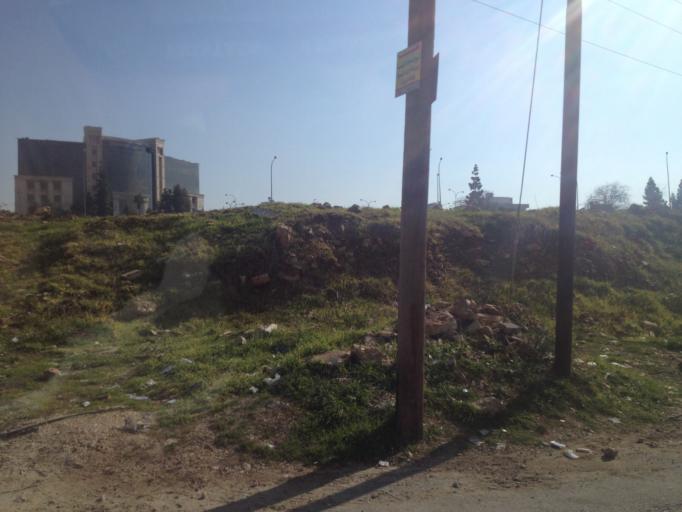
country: JO
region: Amman
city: Wadi as Sir
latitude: 31.9466
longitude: 35.8581
